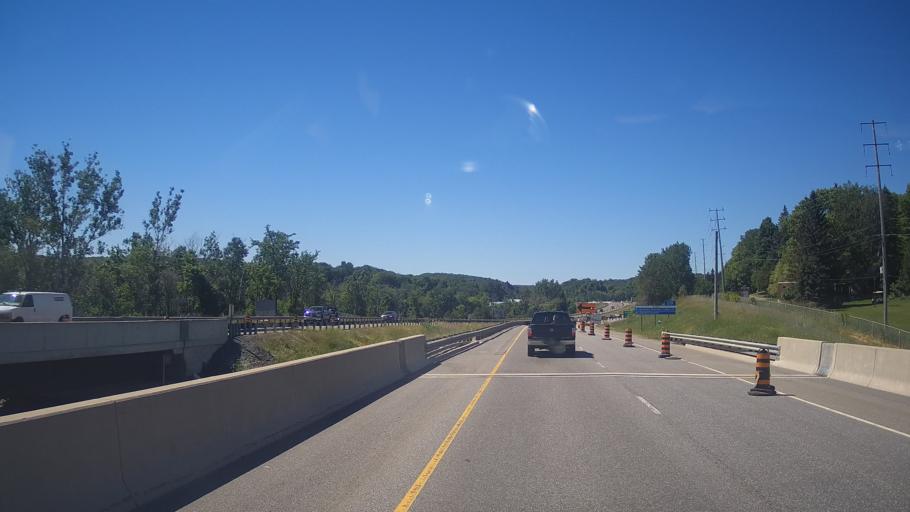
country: CA
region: Ontario
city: Huntsville
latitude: 45.3224
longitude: -79.2405
